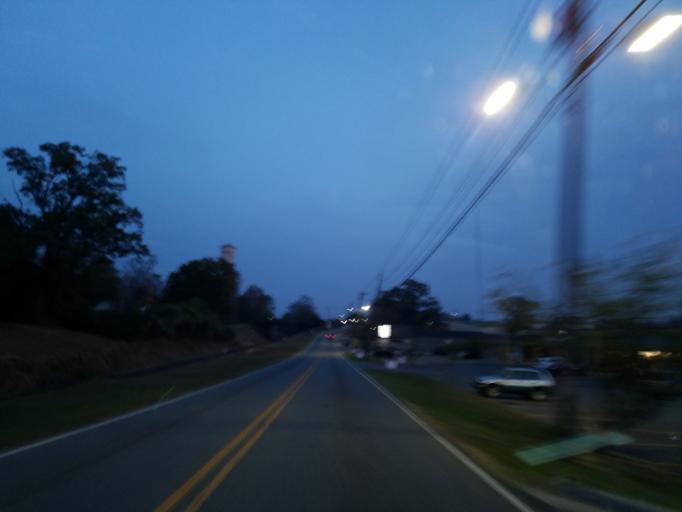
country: US
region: Georgia
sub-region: Pickens County
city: Jasper
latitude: 34.4711
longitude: -84.4339
